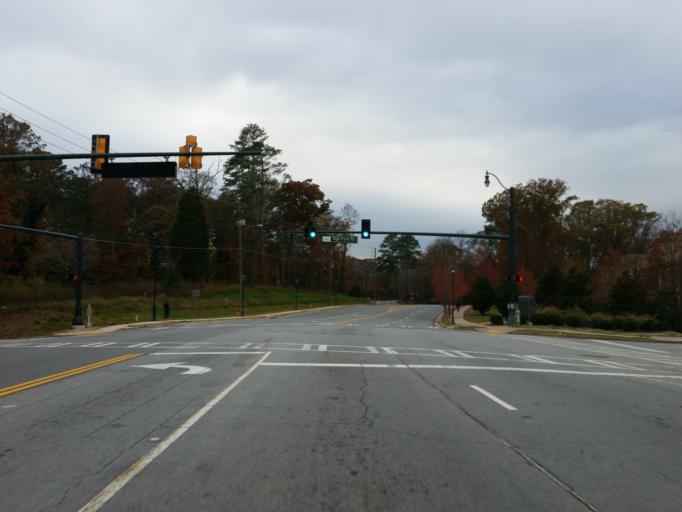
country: US
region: Georgia
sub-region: Fulton County
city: Sandy Springs
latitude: 33.9073
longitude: -84.3643
